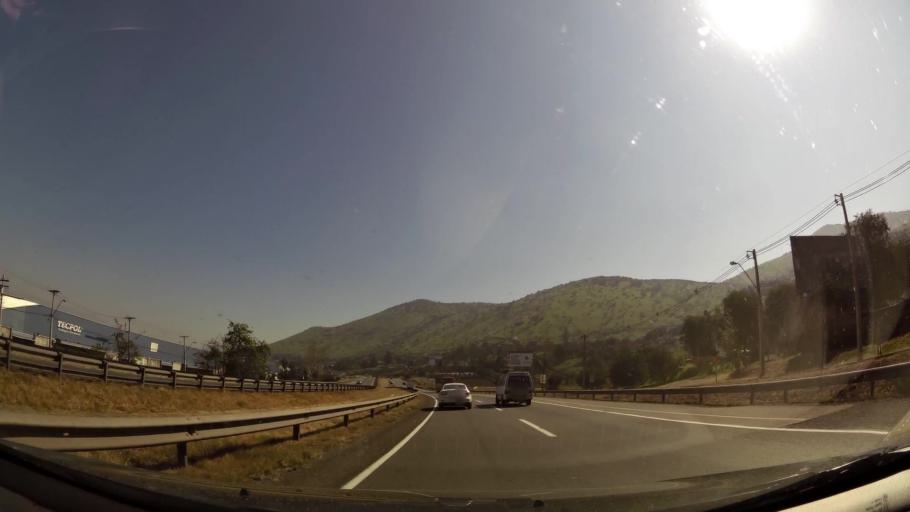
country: CL
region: Santiago Metropolitan
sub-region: Provincia de Chacabuco
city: Chicureo Abajo
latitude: -33.3380
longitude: -70.6923
